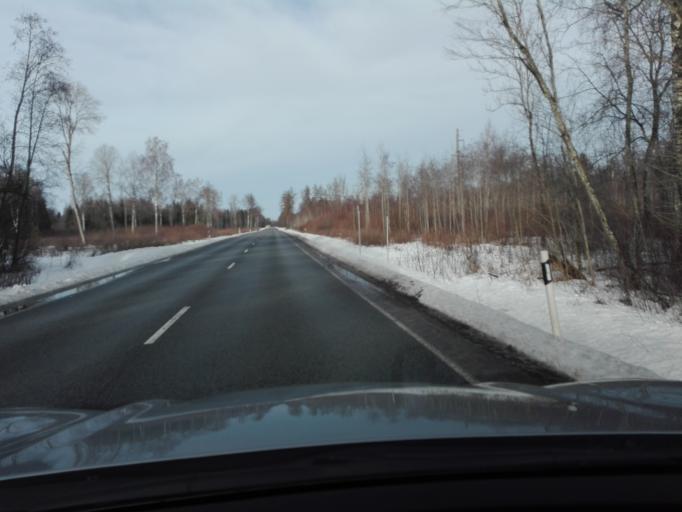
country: EE
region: Raplamaa
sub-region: Rapla vald
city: Rapla
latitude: 58.9232
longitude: 24.7521
